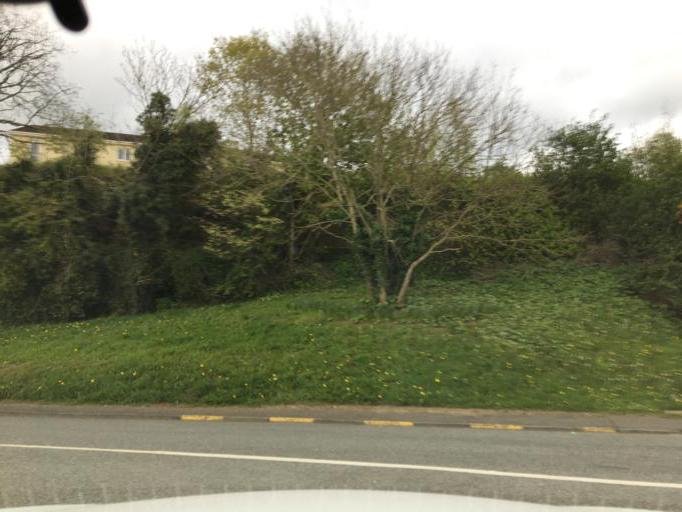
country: IE
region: Leinster
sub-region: Loch Garman
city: New Ross
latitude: 52.3871
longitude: -6.9506
